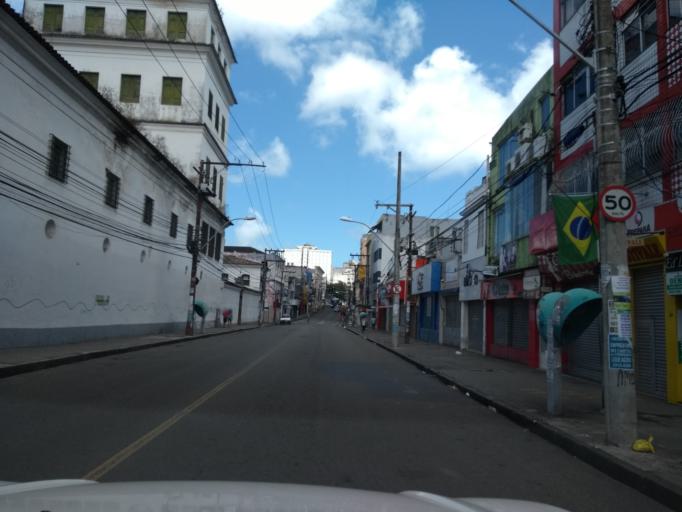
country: BR
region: Bahia
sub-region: Salvador
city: Salvador
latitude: -12.9812
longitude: -38.5126
